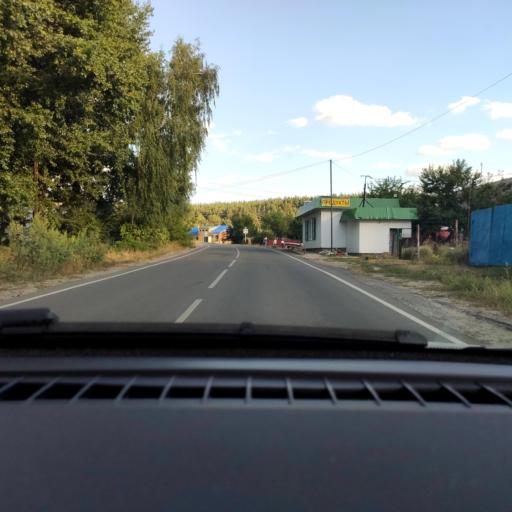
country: RU
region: Voronezj
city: Devitsa
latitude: 51.6551
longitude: 38.9789
